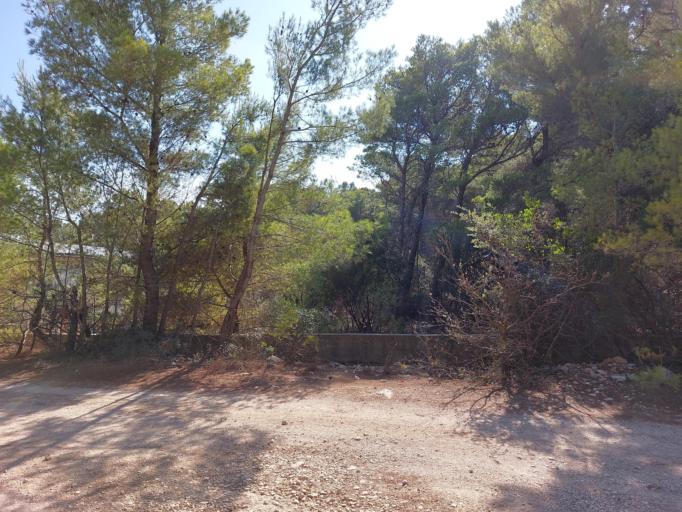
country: HR
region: Dubrovacko-Neretvanska
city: Smokvica
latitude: 42.7381
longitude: 16.8311
